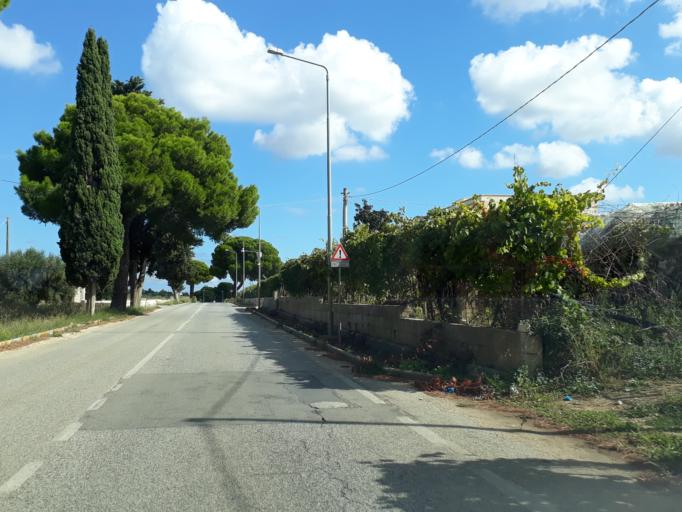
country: IT
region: Apulia
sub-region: Provincia di Bari
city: Rutigliano
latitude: 41.0175
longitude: 17.0200
